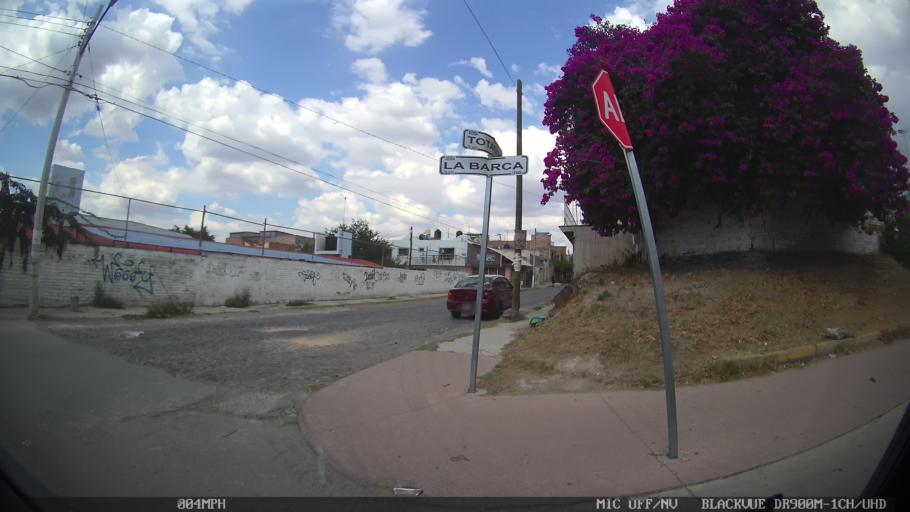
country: MX
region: Jalisco
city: Tlaquepaque
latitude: 20.6835
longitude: -103.2628
